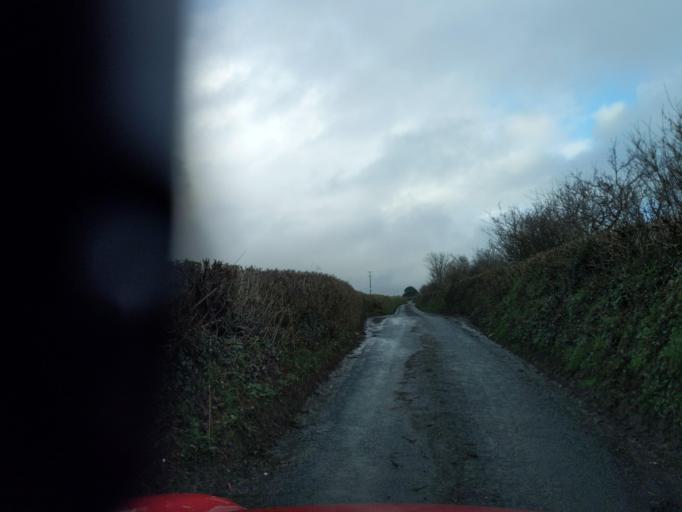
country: GB
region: England
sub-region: Plymouth
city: Plymouth
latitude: 50.4413
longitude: -4.1329
